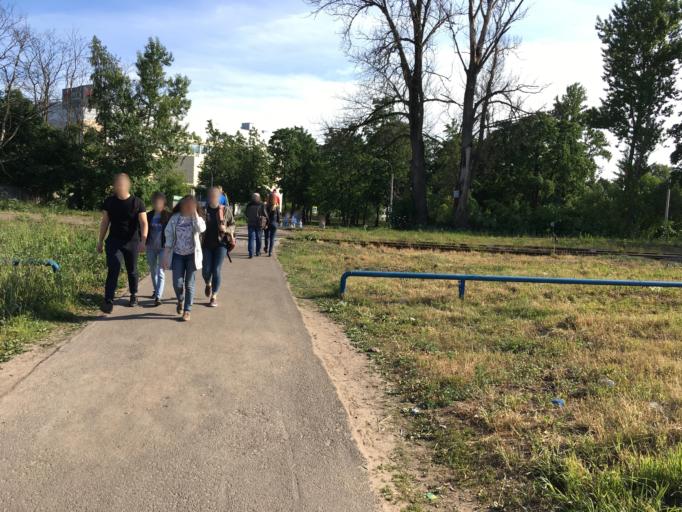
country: RU
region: Leningrad
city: Sampsonievskiy
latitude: 59.9901
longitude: 30.3525
